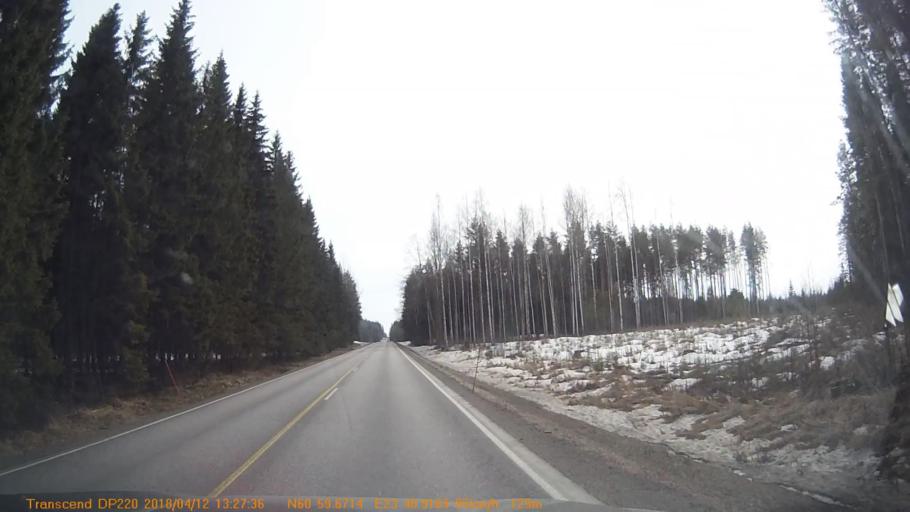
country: FI
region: Pirkanmaa
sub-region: Etelae-Pirkanmaa
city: Kylmaekoski
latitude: 60.9944
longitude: 23.6820
